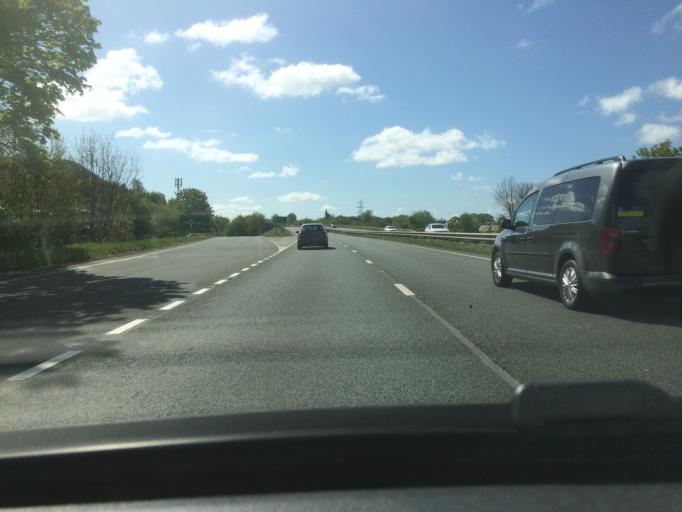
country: GB
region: Wales
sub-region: Wrexham
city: Rhosllanerchrugog
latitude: 53.0293
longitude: -3.0319
